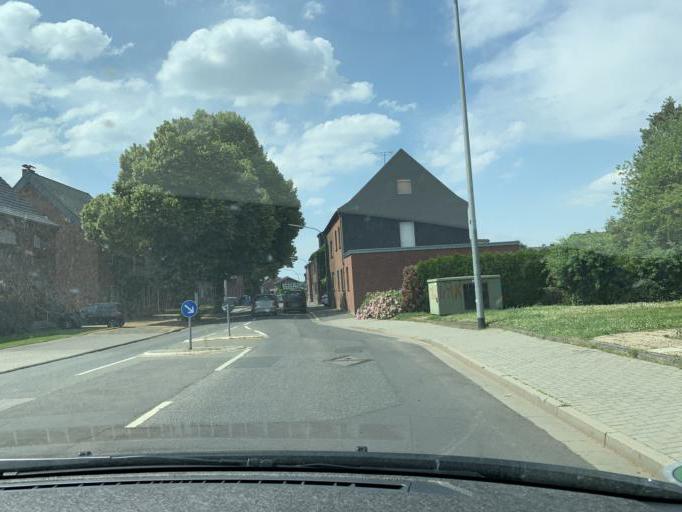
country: DE
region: North Rhine-Westphalia
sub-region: Regierungsbezirk Dusseldorf
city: Grevenbroich
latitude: 51.0422
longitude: 6.5840
